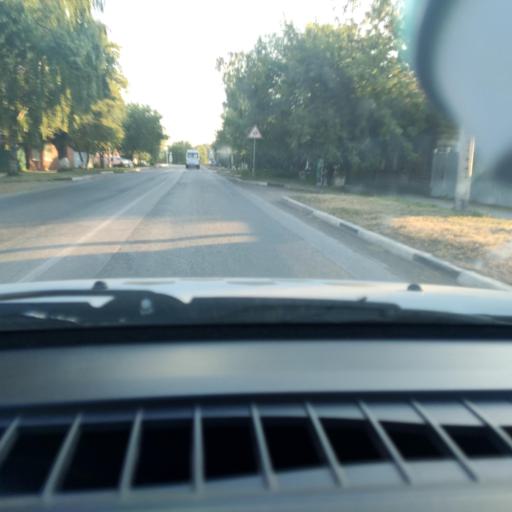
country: RU
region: Perm
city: Kungur
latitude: 57.4412
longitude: 56.9530
